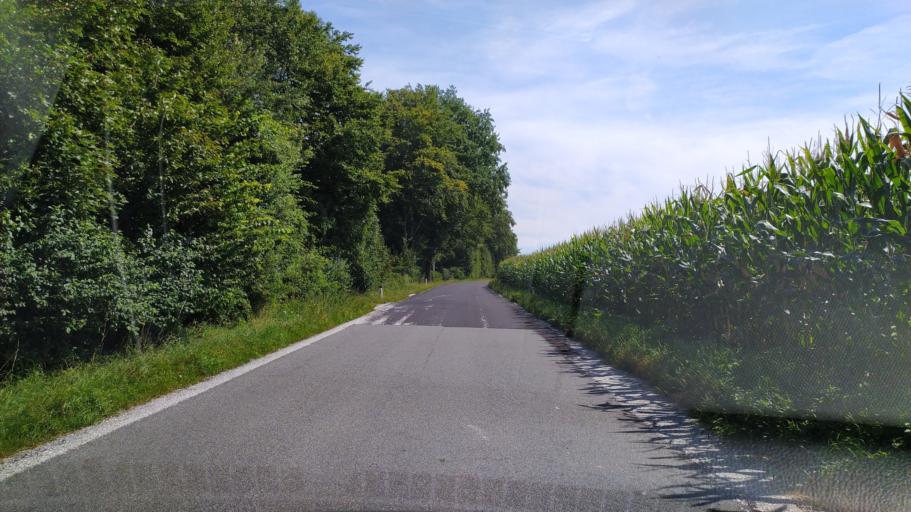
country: AT
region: Lower Austria
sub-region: Politischer Bezirk Amstetten
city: Strengberg
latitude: 48.1196
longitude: 14.6473
